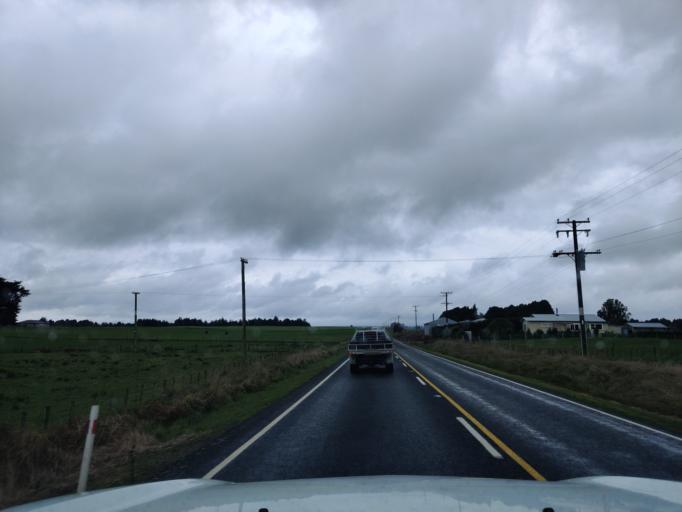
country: NZ
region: Manawatu-Wanganui
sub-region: Ruapehu District
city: Waiouru
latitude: -39.3607
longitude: 175.3468
